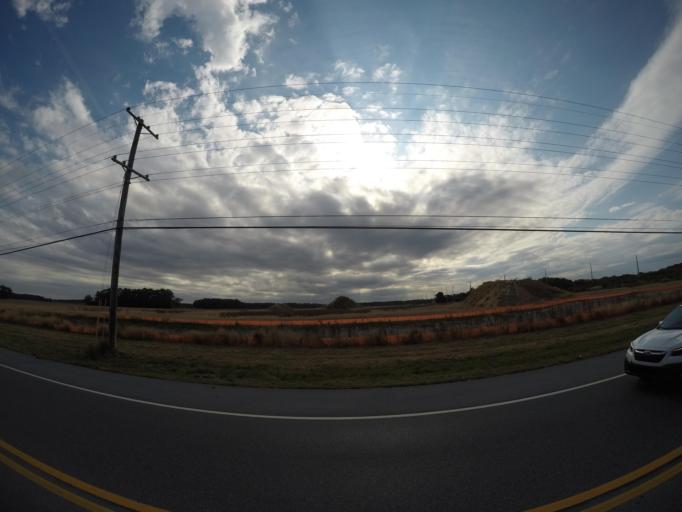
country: US
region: Delaware
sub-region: Sussex County
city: Lewes
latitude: 38.7314
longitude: -75.1515
